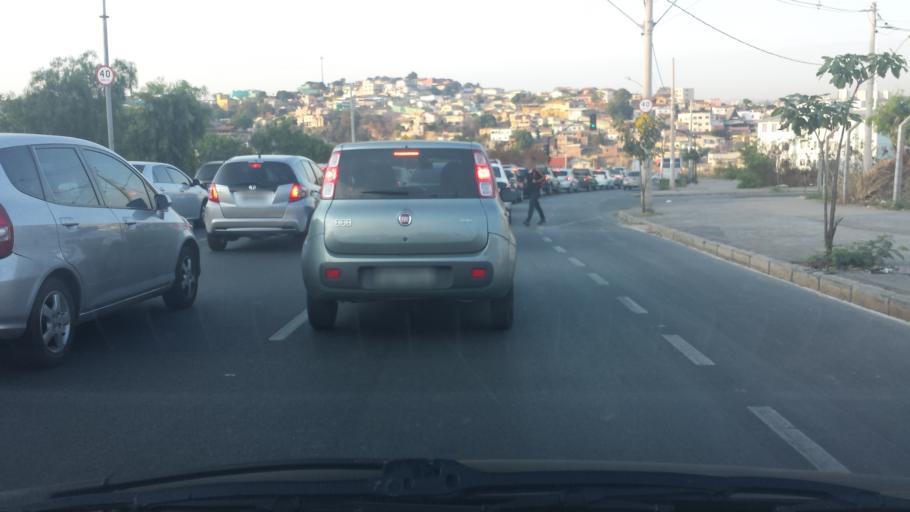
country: BR
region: Minas Gerais
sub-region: Belo Horizonte
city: Belo Horizonte
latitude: -19.8986
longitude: -43.9925
